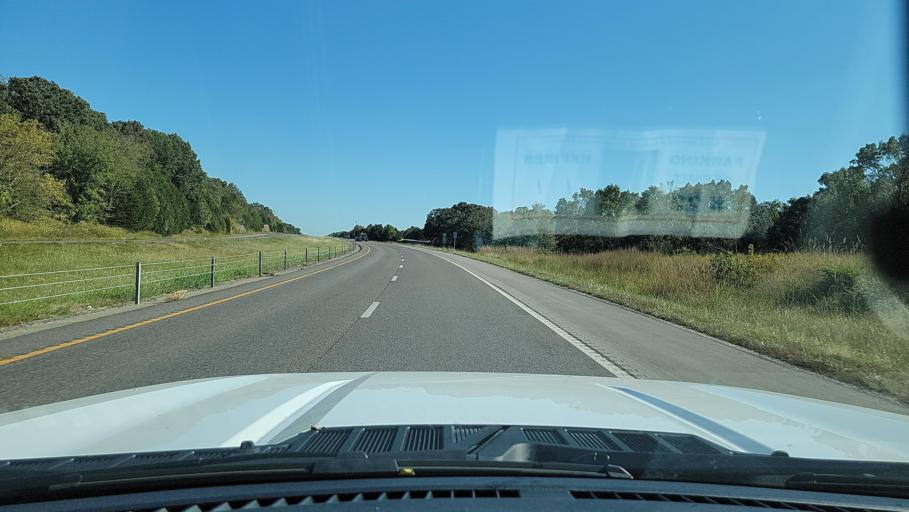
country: US
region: Missouri
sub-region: Sainte Genevieve County
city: Sainte Genevieve
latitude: 37.9692
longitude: -90.1858
